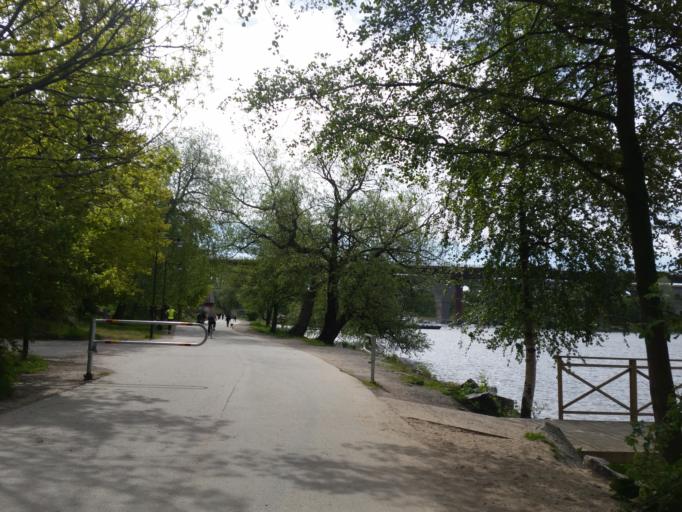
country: SE
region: Stockholm
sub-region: Stockholms Kommun
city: Arsta
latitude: 59.3118
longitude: 18.0388
